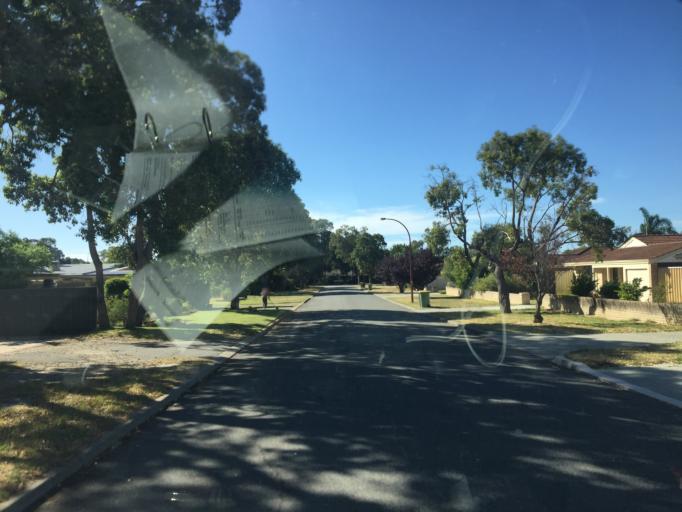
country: AU
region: Western Australia
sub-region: Gosnells
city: Maddington
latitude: -32.0581
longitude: 116.0017
